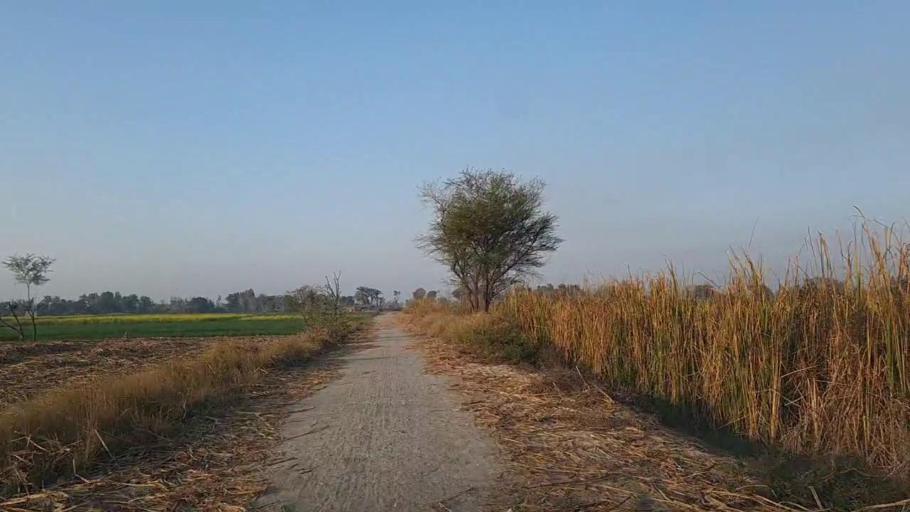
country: PK
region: Sindh
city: Daur
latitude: 26.4863
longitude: 68.4181
